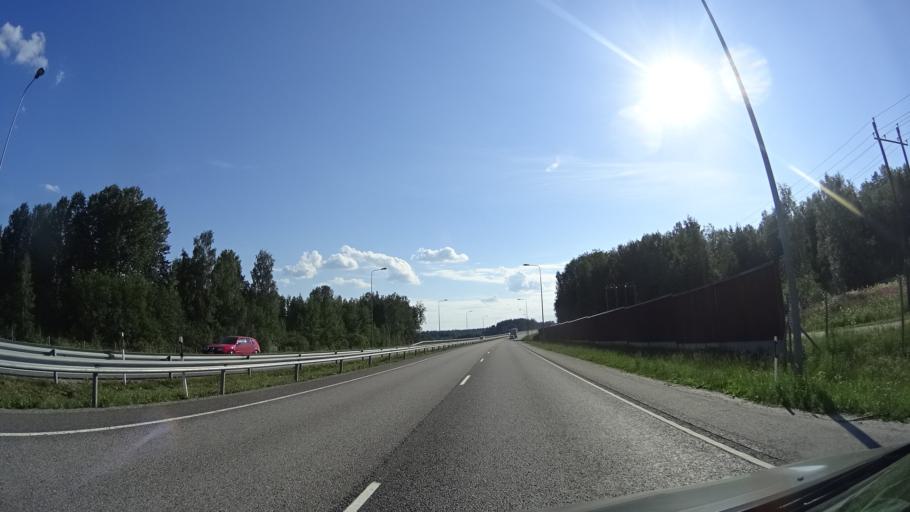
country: FI
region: South Karelia
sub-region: Imatra
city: Imatra
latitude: 61.1685
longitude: 28.6881
